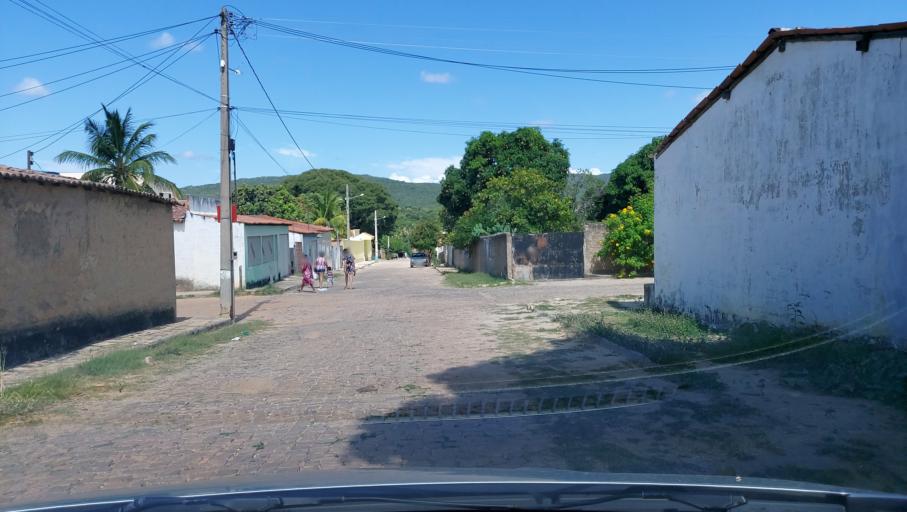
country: BR
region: Bahia
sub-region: Oliveira Dos Brejinhos
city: Beira Rio
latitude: -11.9972
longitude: -42.6309
